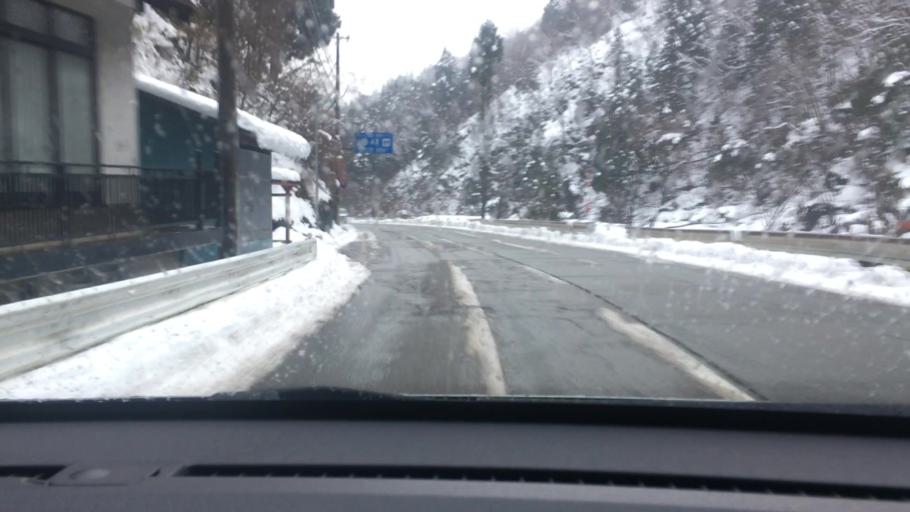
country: JP
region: Hyogo
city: Toyooka
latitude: 35.3705
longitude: 134.5773
